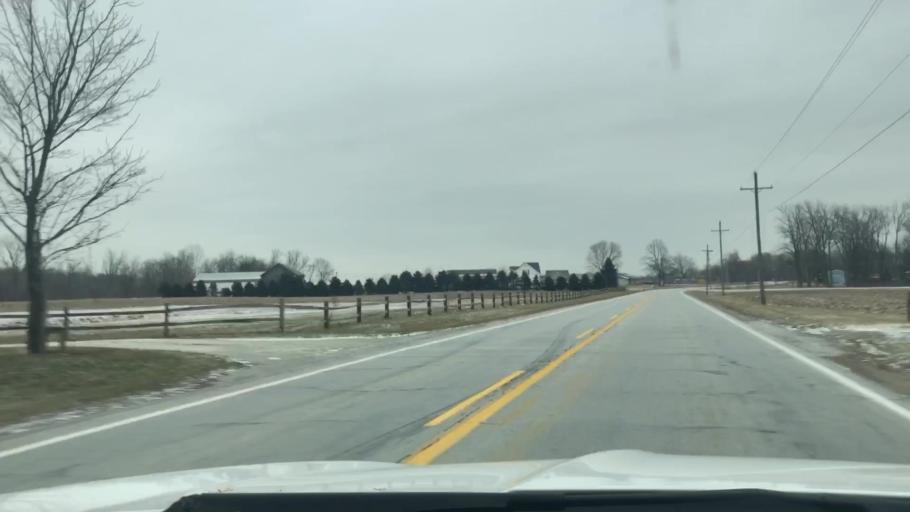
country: US
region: Indiana
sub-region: Fulton County
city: Rochester
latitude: 41.0564
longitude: -86.1617
